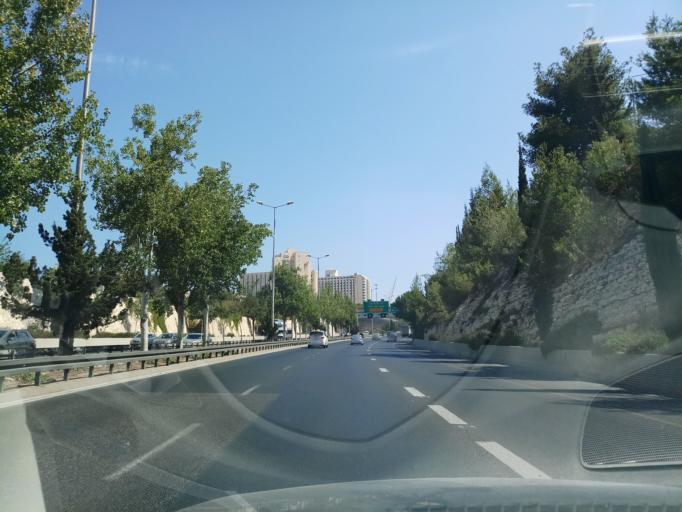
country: IL
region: Jerusalem
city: Jerusalem
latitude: 31.7786
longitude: 35.1944
